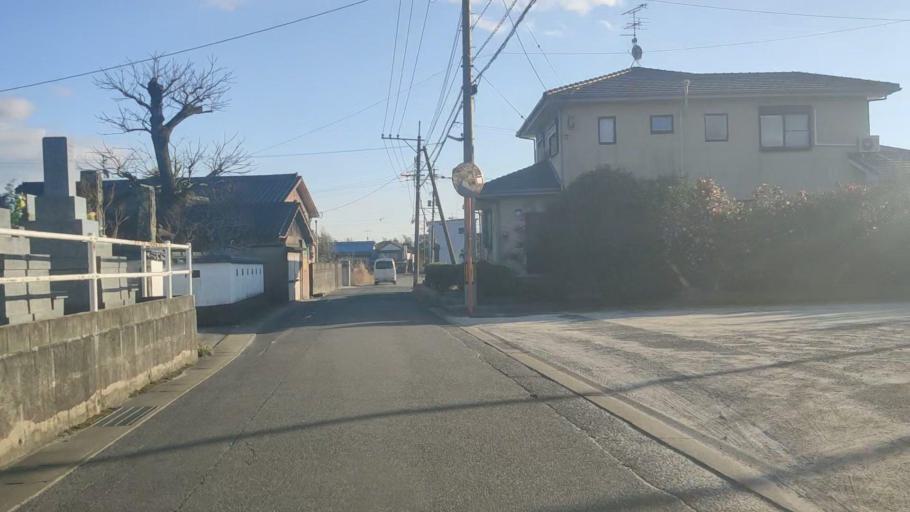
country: JP
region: Saga Prefecture
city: Saga-shi
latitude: 33.2932
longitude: 130.2403
